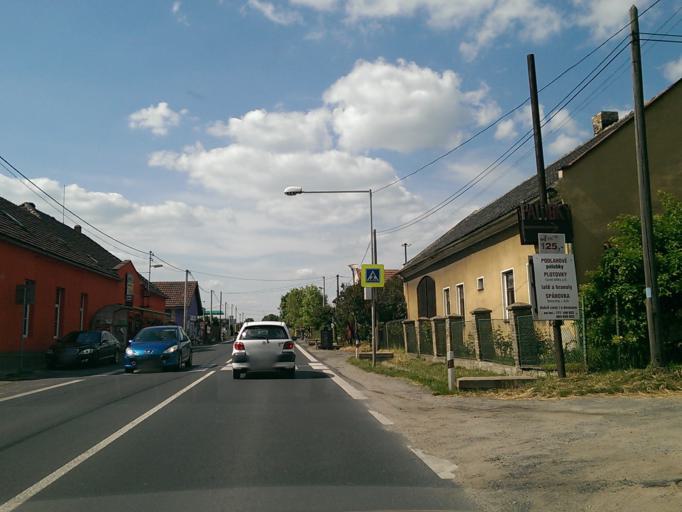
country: CZ
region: Central Bohemia
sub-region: Okres Melnik
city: Melnik
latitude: 50.3209
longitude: 14.5066
